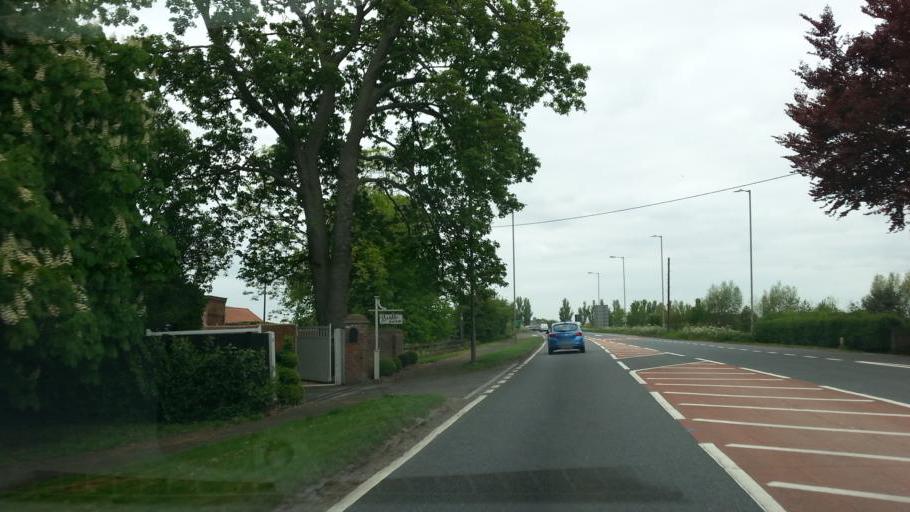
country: GB
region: England
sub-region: Lincolnshire
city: Donington
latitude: 52.9706
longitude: -0.1893
